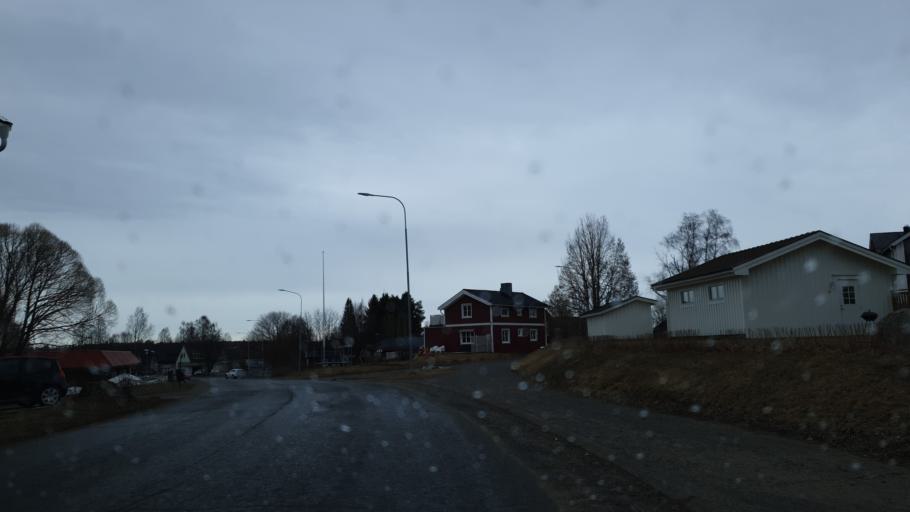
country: SE
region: Vaesterbotten
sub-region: Skelleftea Kommun
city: Kage
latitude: 64.8310
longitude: 20.9882
